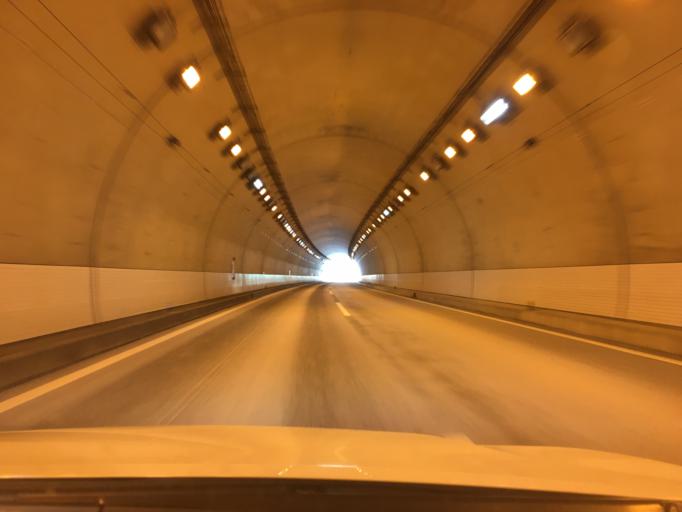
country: JP
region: Yamagata
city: Yamagata-shi
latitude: 38.2573
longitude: 140.3680
